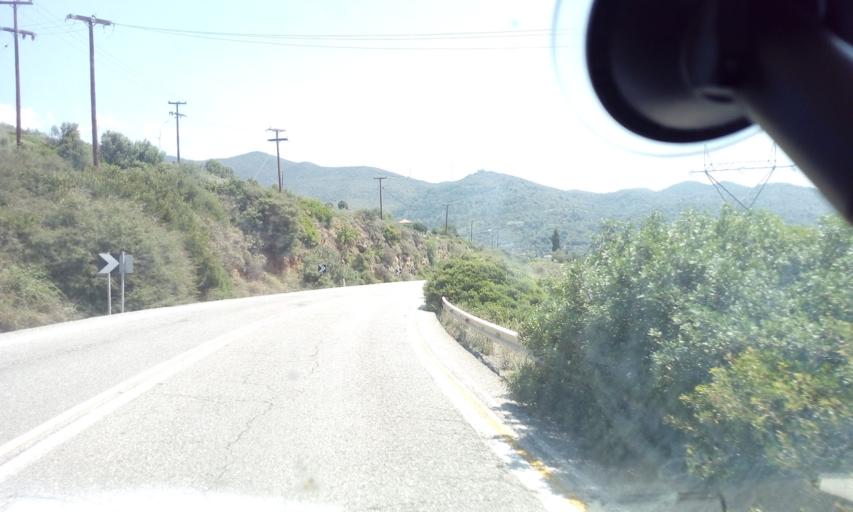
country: GR
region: West Greece
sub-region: Nomos Aitolias kai Akarnanias
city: Antirrio
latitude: 38.3550
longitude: 21.6988
